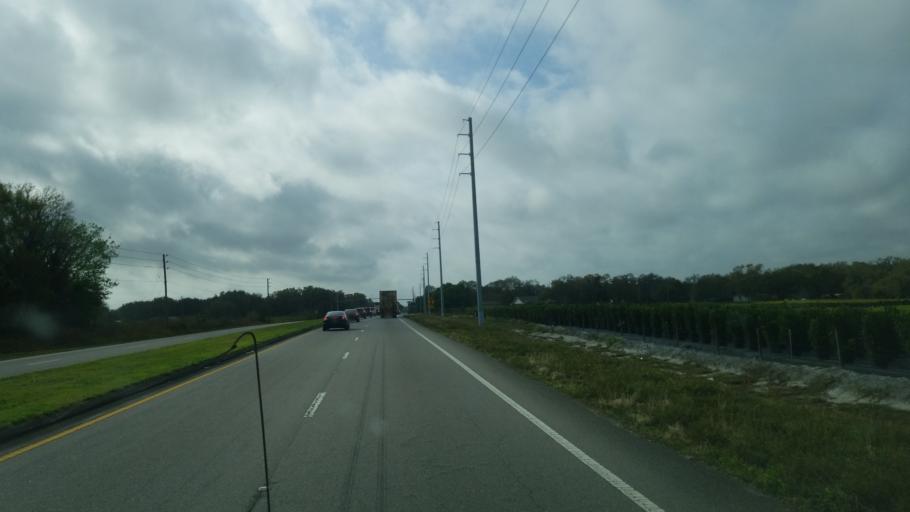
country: US
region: Florida
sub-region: Polk County
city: Willow Oak
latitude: 27.9557
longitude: -82.0555
